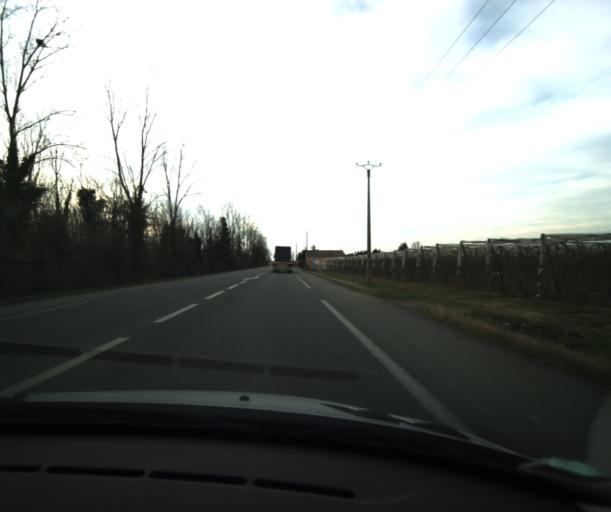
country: FR
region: Midi-Pyrenees
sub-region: Departement du Tarn-et-Garonne
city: Castelsarrasin
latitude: 44.0298
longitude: 1.1331
